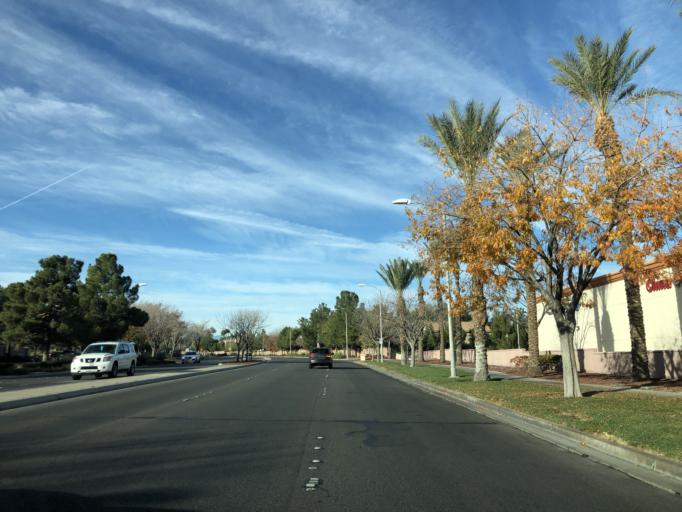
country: US
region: Nevada
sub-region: Clark County
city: Whitney
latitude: 36.0238
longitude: -115.0629
